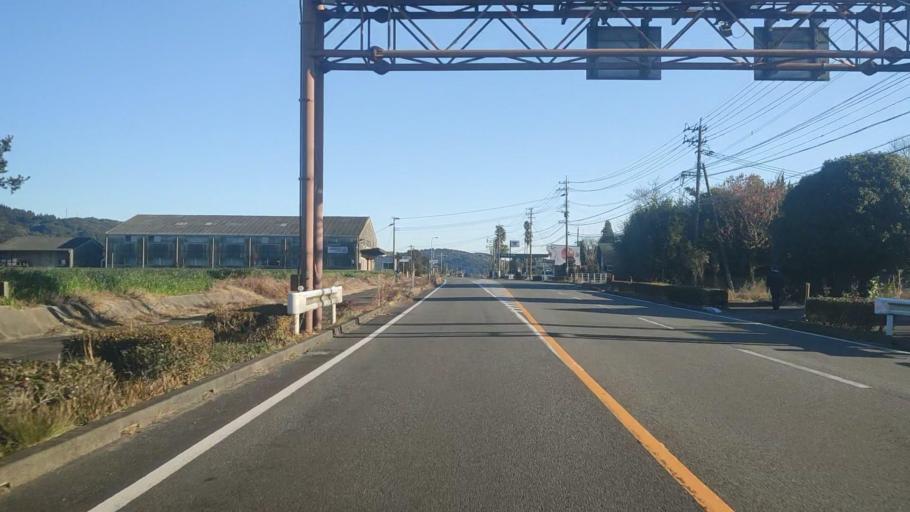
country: JP
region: Miyazaki
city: Takanabe
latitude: 32.3229
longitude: 131.5969
